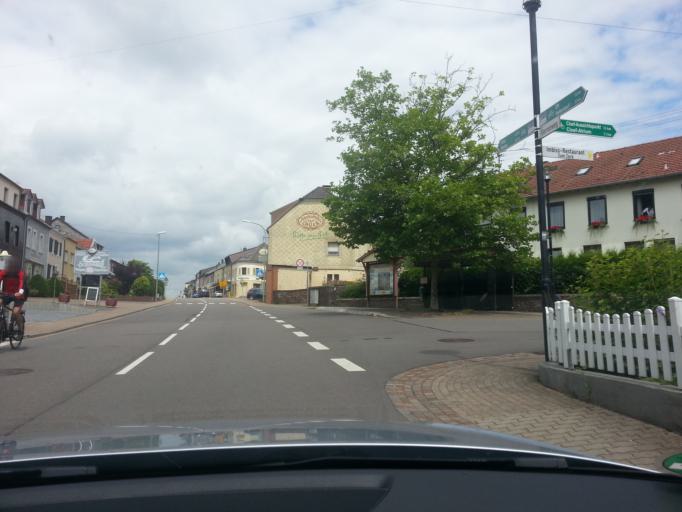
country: DE
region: Saarland
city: Orscholz
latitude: 49.5047
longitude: 6.5238
